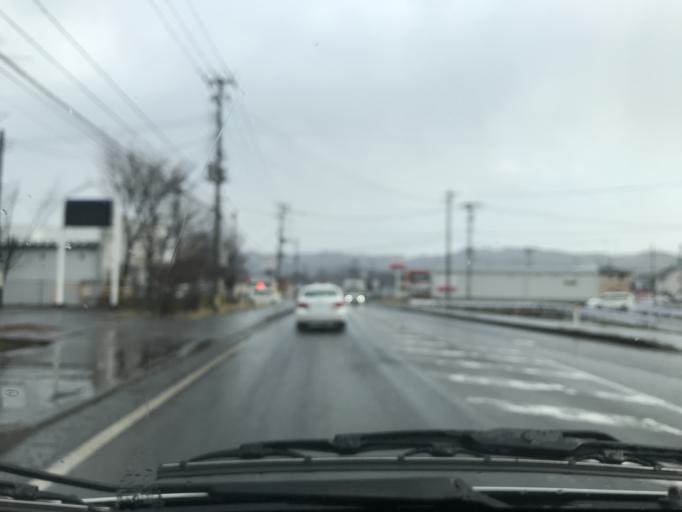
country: JP
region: Iwate
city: Kitakami
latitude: 39.2938
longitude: 141.1350
